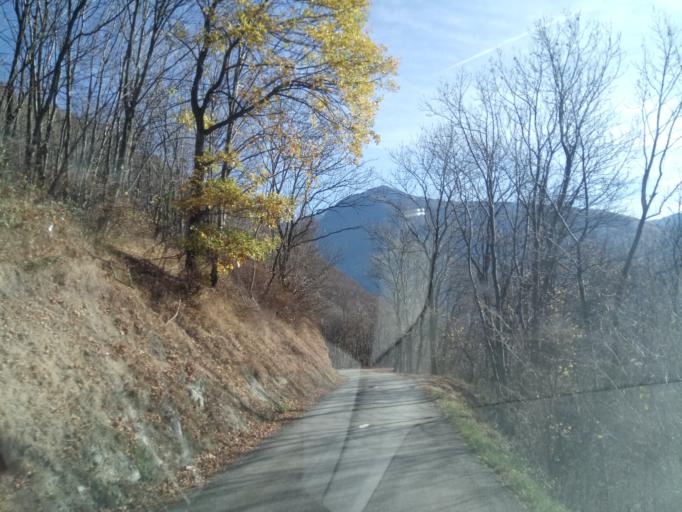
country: FR
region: Rhone-Alpes
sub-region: Departement de la Savoie
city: Saint-Michel-de-Maurienne
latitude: 45.2300
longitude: 6.4789
